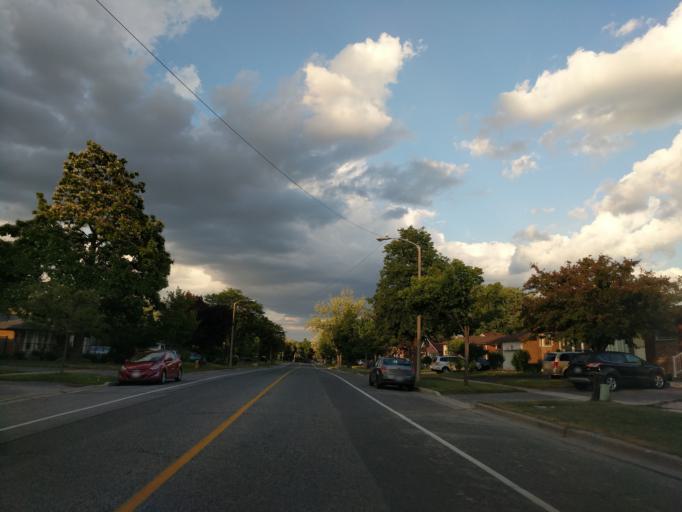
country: CA
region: Ontario
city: Scarborough
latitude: 43.7976
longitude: -79.2813
